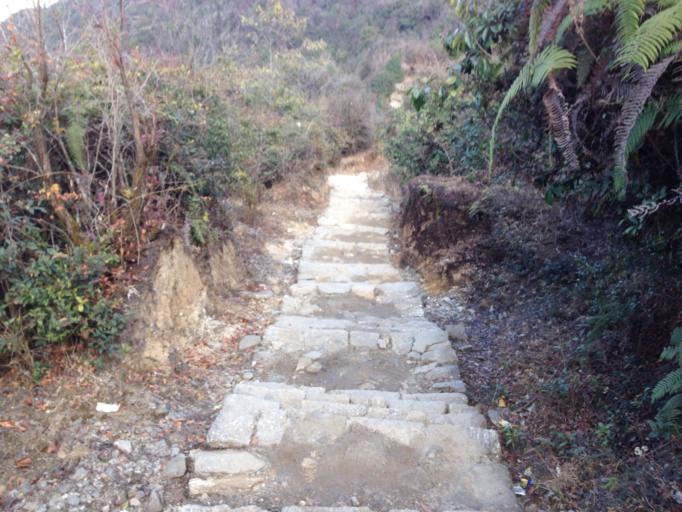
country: NP
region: Central Region
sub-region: Bagmati Zone
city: Nagarkot
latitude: 27.8148
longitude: 85.4462
